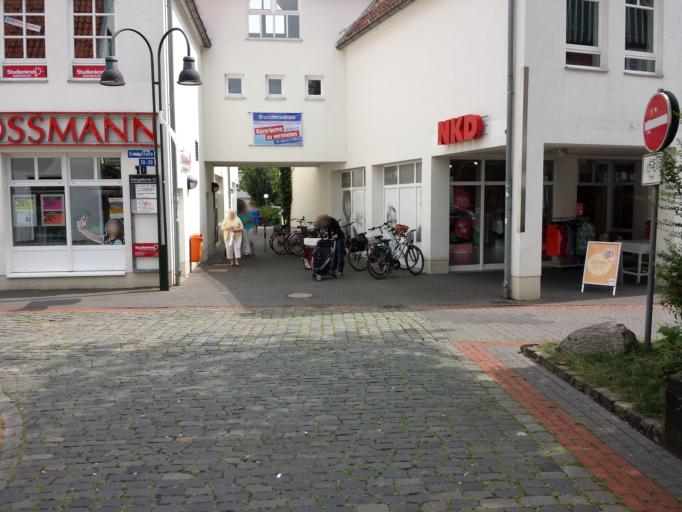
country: DE
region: North Rhine-Westphalia
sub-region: Regierungsbezirk Detmold
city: Rheda-Wiedenbruck
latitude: 51.8333
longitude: 8.3105
